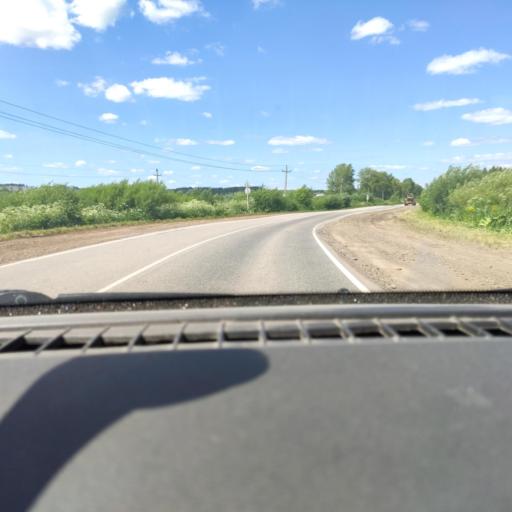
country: RU
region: Perm
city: Chaykovskaya
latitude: 58.0950
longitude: 55.5952
